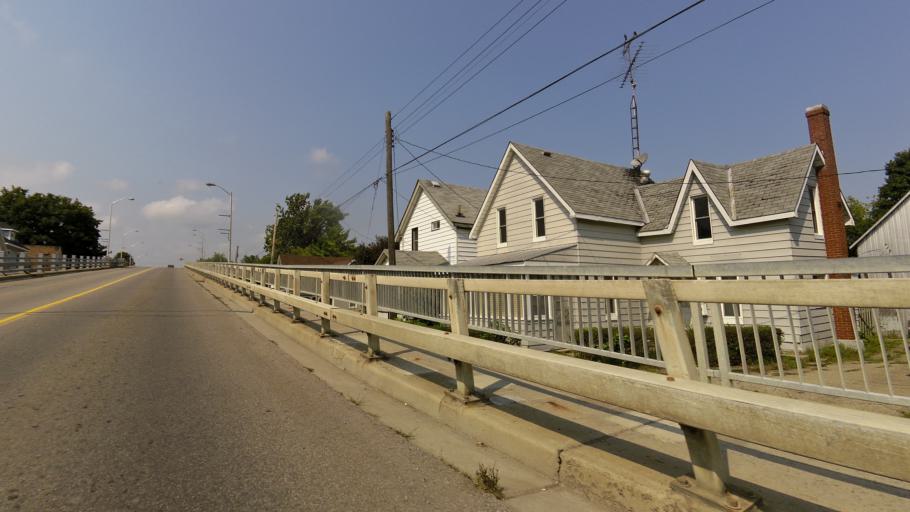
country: CA
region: Ontario
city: Prescott
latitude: 44.7141
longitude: -75.5171
